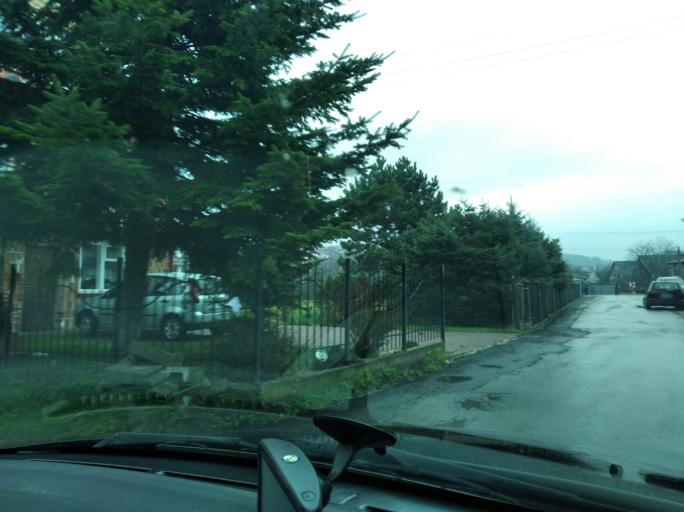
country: PL
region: Subcarpathian Voivodeship
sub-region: Powiat strzyzowski
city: Czudec
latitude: 49.9444
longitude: 21.8398
